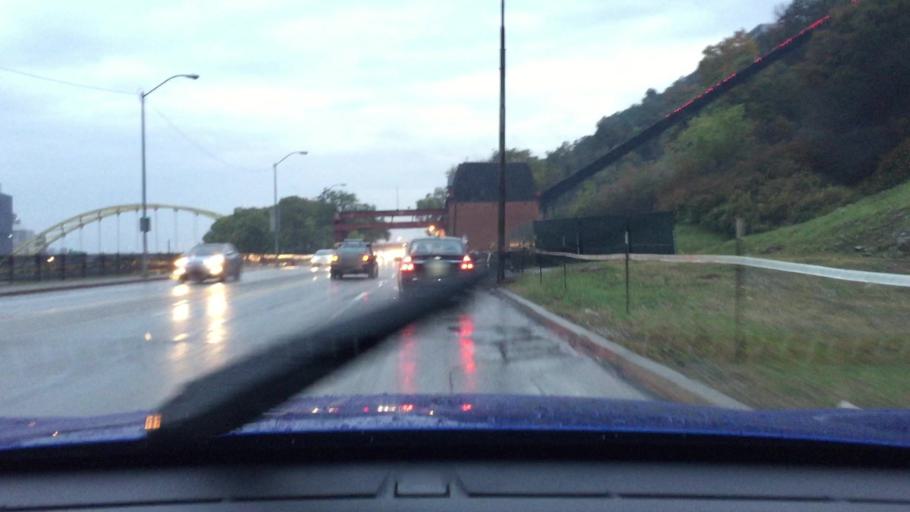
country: US
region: Pennsylvania
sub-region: Allegheny County
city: Pittsburgh
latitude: 40.4406
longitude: -80.0188
